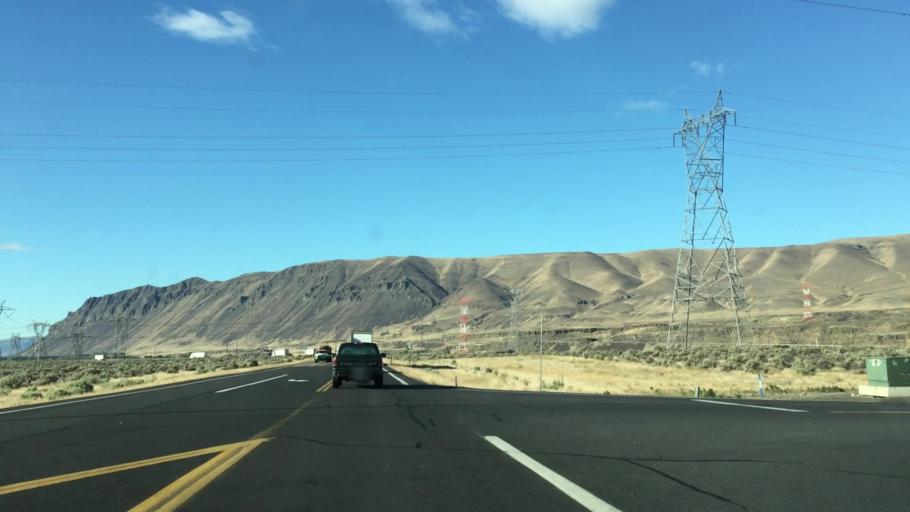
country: US
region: Washington
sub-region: Grant County
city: Mattawa
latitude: 46.8755
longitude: -119.9557
